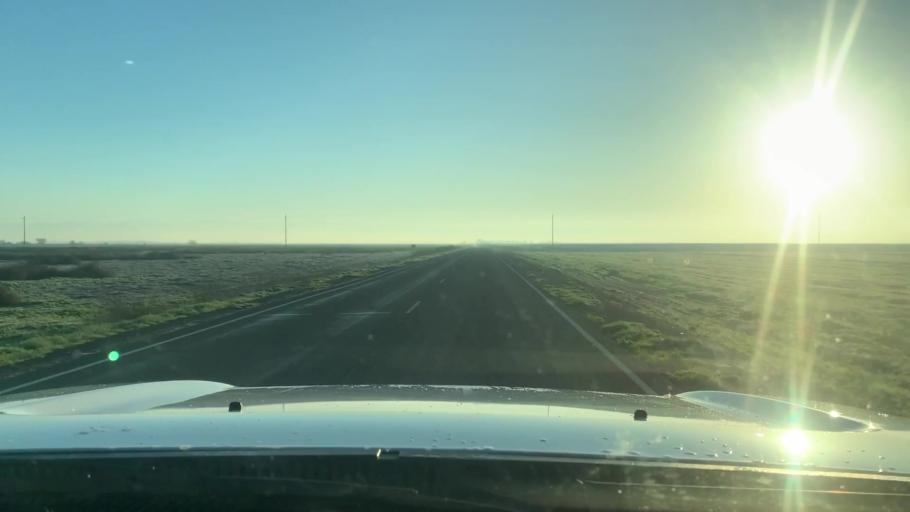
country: US
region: California
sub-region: Kings County
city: Stratford
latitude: 36.2111
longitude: -119.7477
